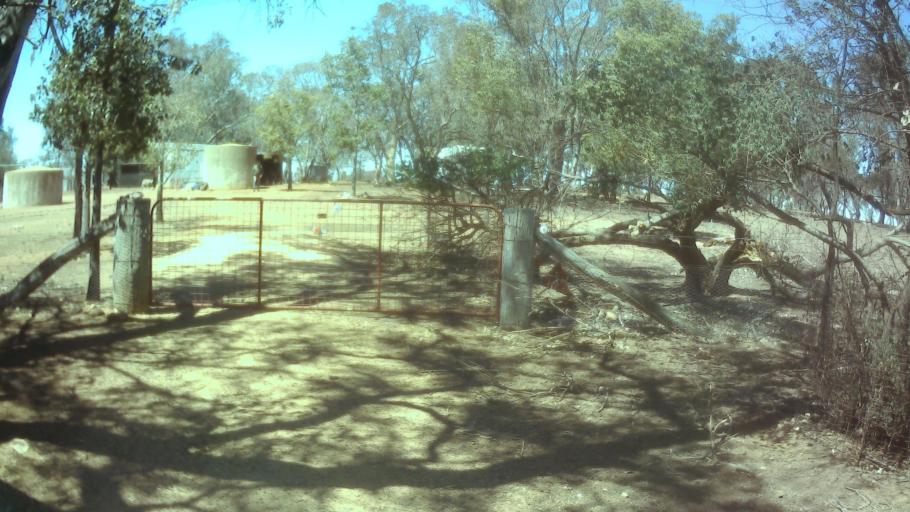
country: AU
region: New South Wales
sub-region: Cowra
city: Cowra
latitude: -33.9098
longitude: 148.5055
